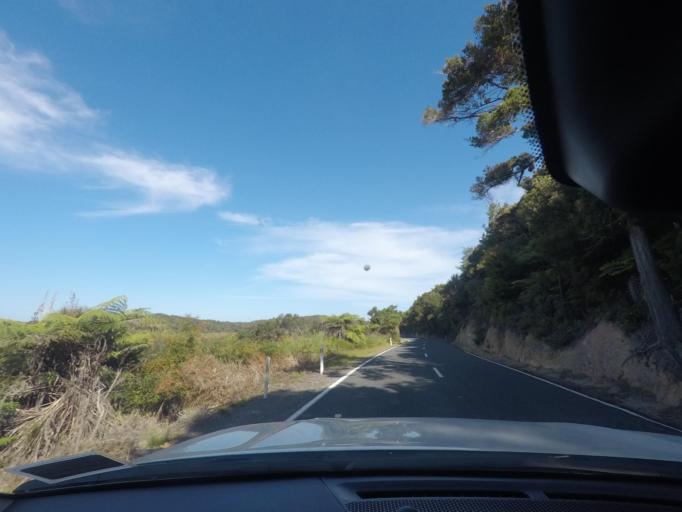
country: NZ
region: Northland
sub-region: Whangarei
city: Ngunguru
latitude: -35.6639
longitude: 174.4821
